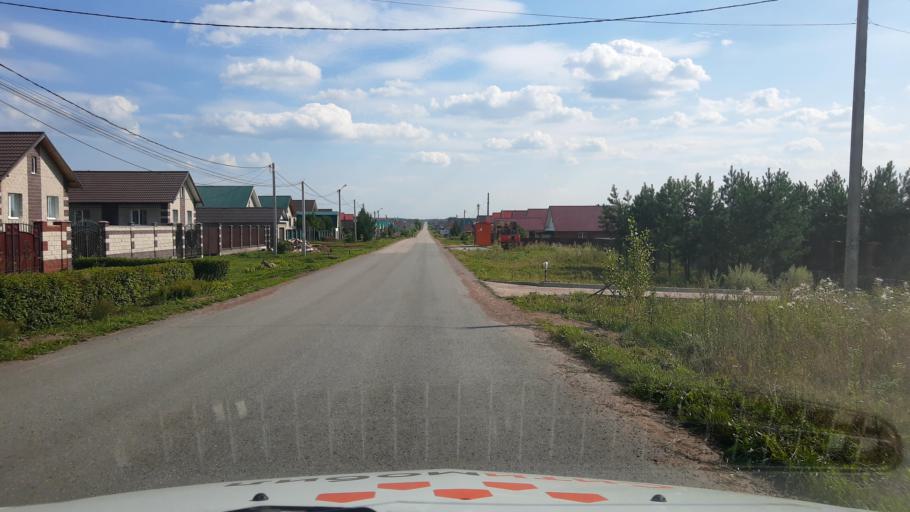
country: RU
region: Bashkortostan
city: Kabakovo
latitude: 54.6663
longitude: 56.2138
